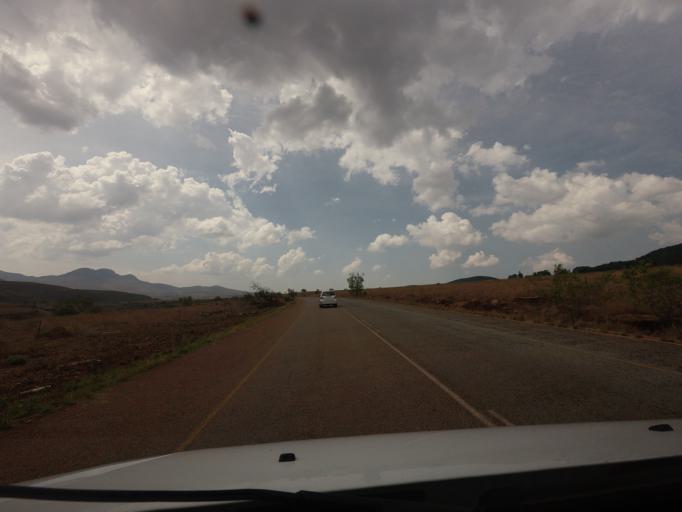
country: ZA
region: Mpumalanga
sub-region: Ehlanzeni District
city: Graksop
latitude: -24.7008
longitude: 30.8199
